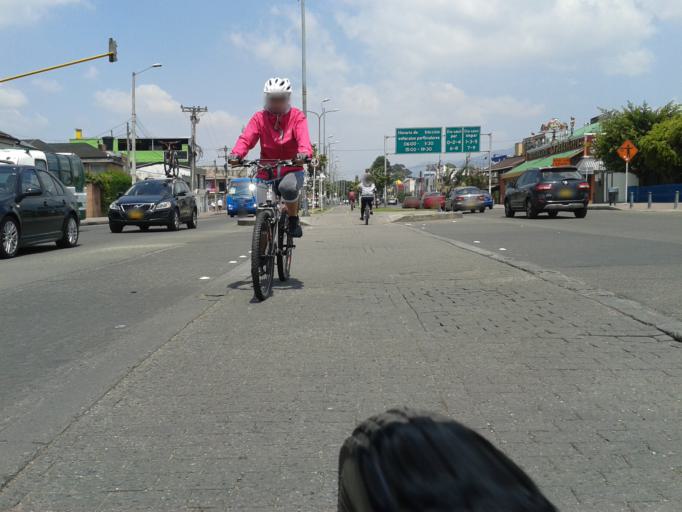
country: CO
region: Bogota D.C.
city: Barrio San Luis
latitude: 4.7297
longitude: -74.0453
